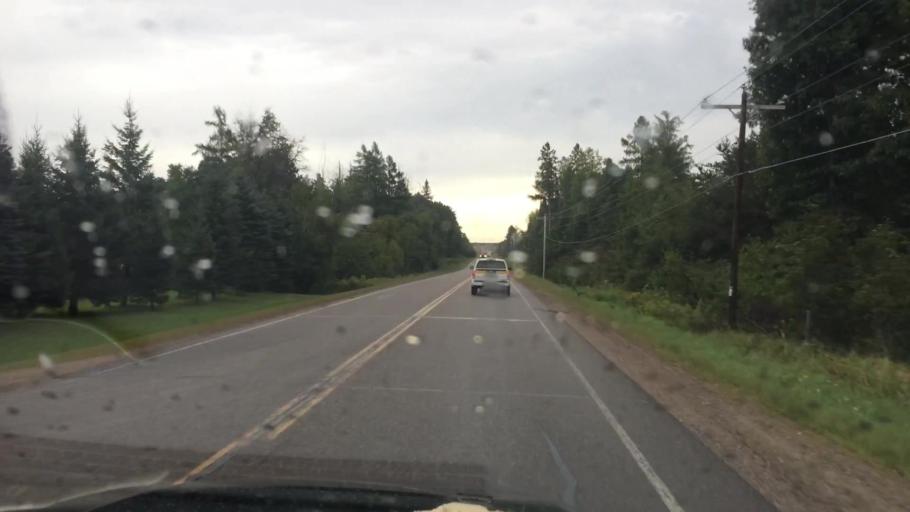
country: US
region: Wisconsin
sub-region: Lincoln County
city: Tomahawk
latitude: 45.4962
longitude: -89.7157
